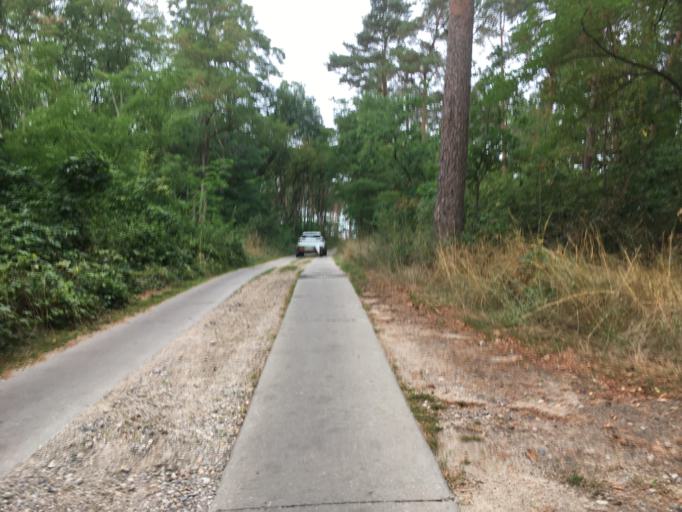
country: DE
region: Brandenburg
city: Gerswalde
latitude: 53.1935
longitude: 13.8321
